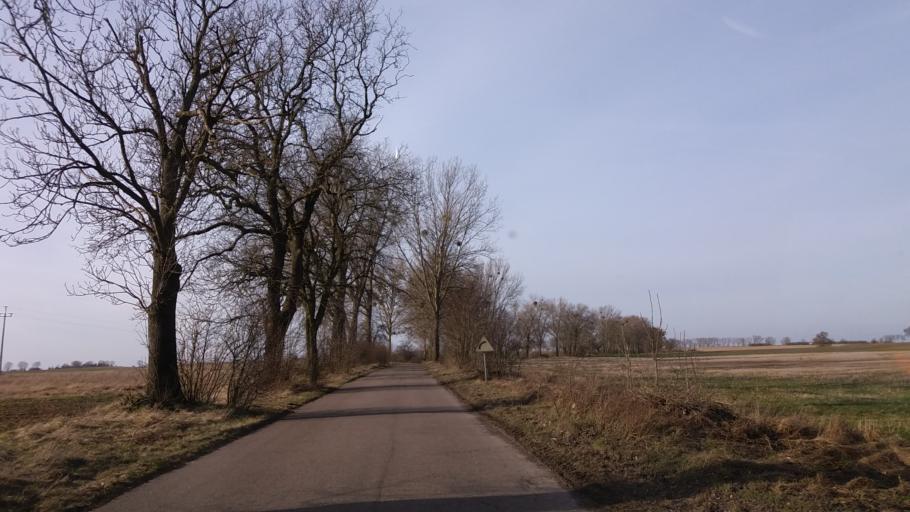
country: PL
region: West Pomeranian Voivodeship
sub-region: Powiat choszczenski
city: Choszczno
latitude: 53.1136
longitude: 15.4010
